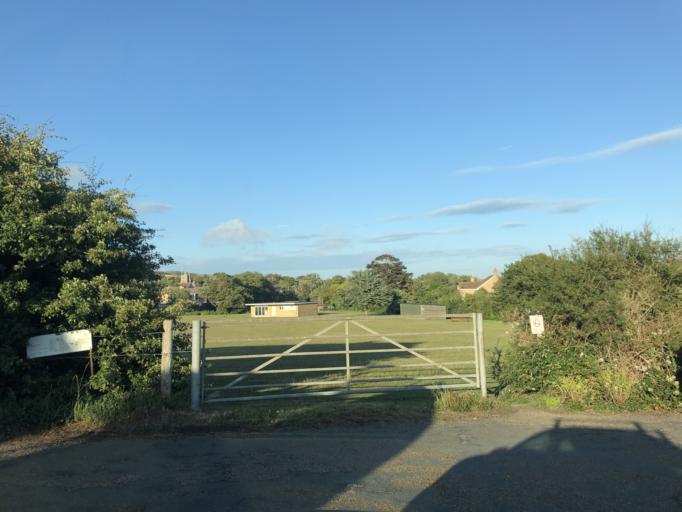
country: GB
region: England
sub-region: Isle of Wight
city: Shalfleet
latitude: 50.6412
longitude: -1.4005
